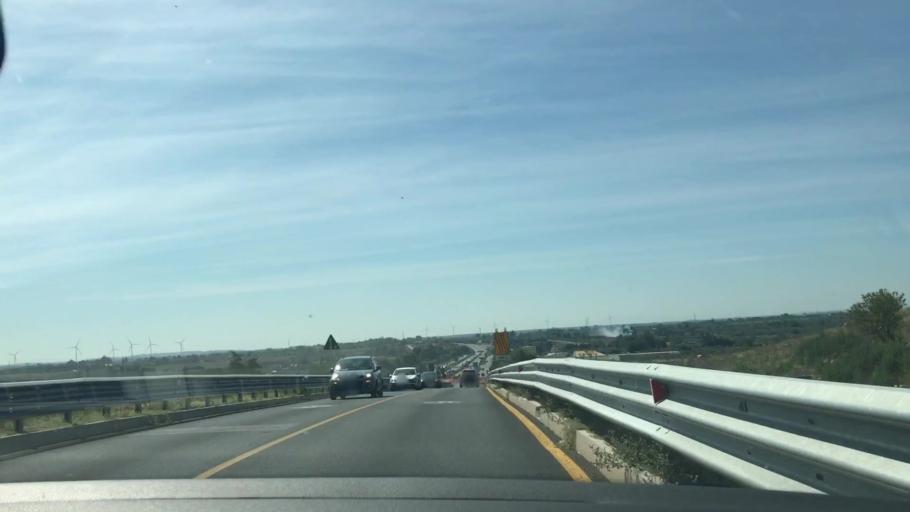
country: IT
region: Apulia
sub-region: Provincia di Bari
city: Altamura
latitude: 40.8086
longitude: 16.5557
